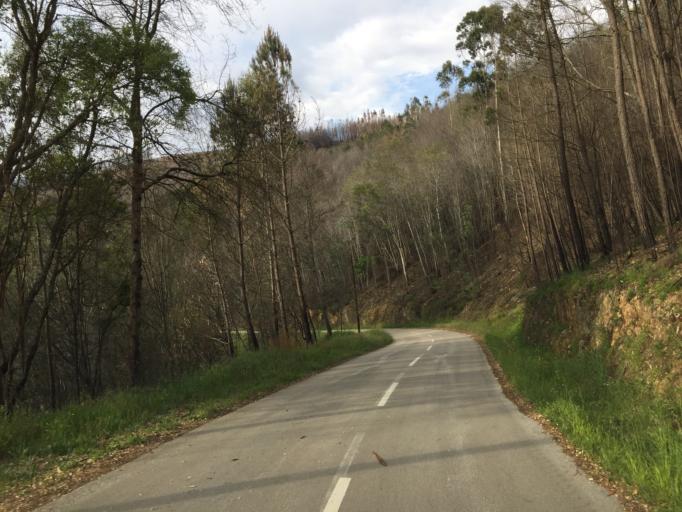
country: PT
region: Coimbra
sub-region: Arganil
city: Arganil
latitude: 40.1410
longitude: -8.0096
